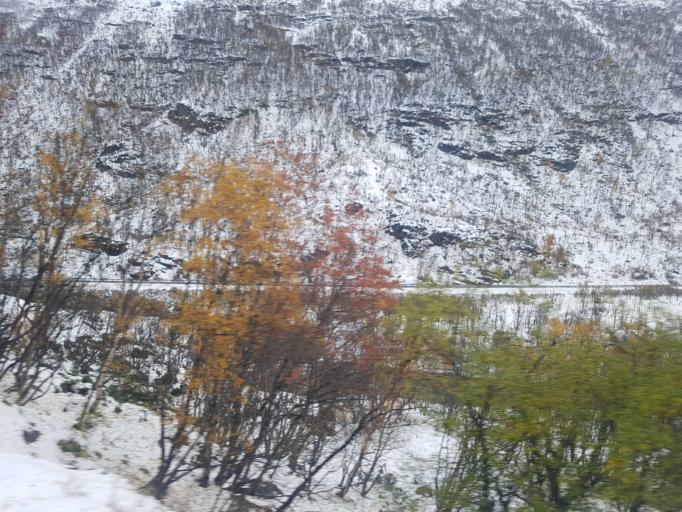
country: NO
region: Sor-Trondelag
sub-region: Oppdal
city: Oppdal
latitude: 62.3342
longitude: 9.6222
